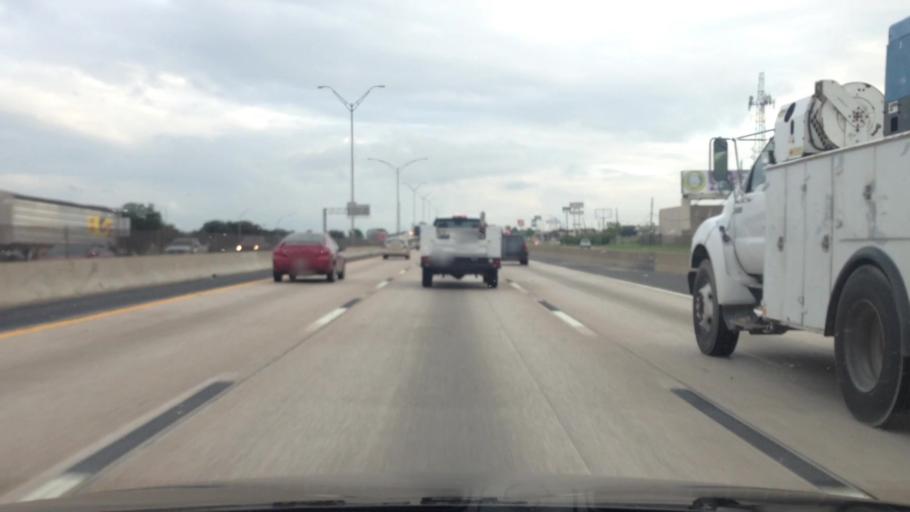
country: US
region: Texas
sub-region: Tarrant County
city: Edgecliff Village
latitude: 32.6407
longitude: -97.3215
